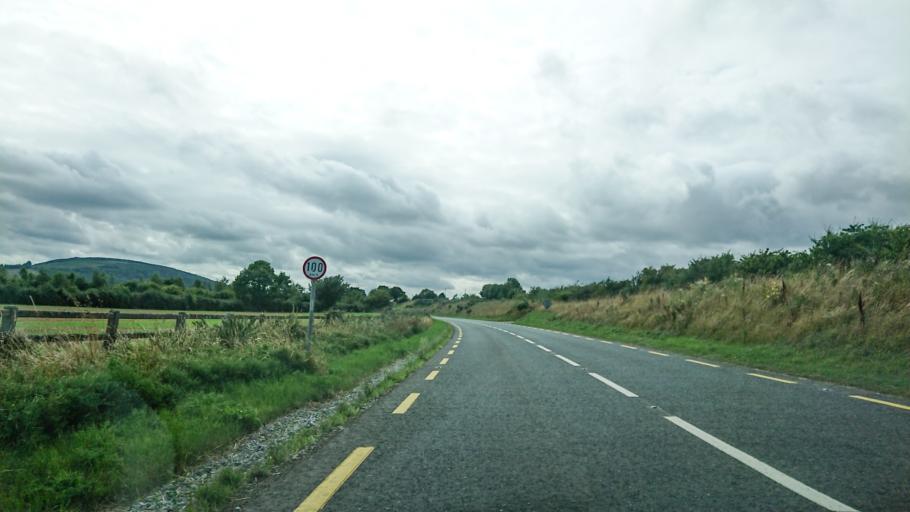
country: IE
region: Munster
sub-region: County Cork
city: Mallow
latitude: 52.1547
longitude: -8.5193
